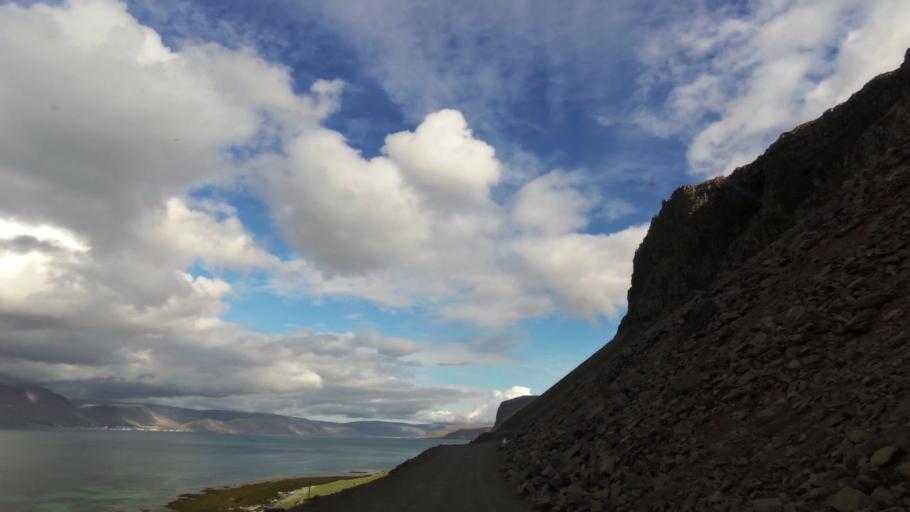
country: IS
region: West
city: Olafsvik
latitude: 65.6017
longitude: -24.1440
